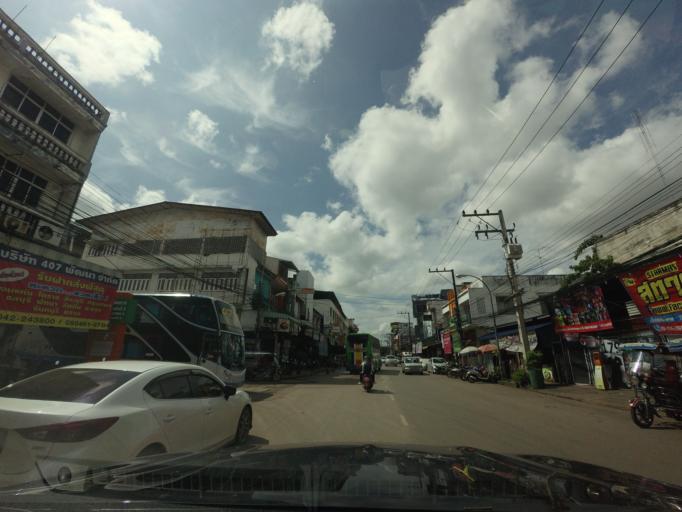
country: TH
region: Changwat Udon Thani
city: Udon Thani
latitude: 17.4031
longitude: 102.7996
